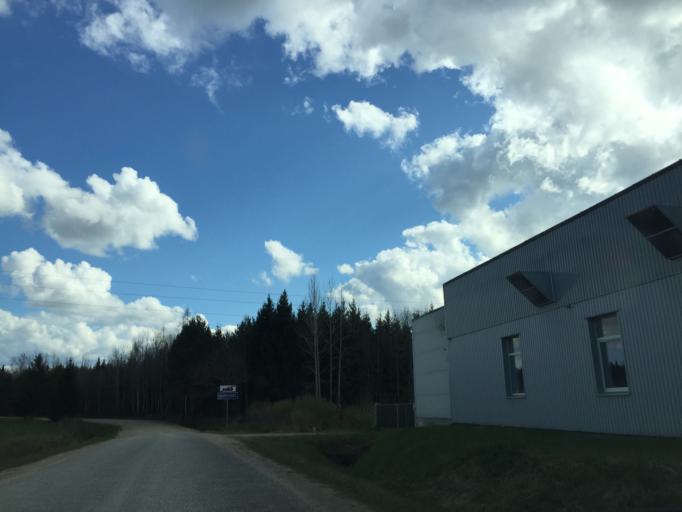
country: LV
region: Beverina
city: Murmuiza
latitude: 57.4669
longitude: 25.4985
